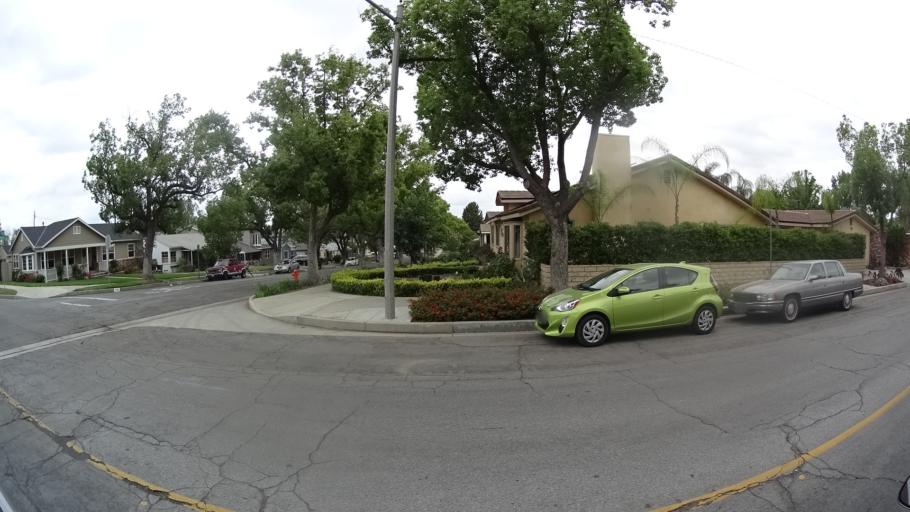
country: US
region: California
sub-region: Los Angeles County
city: Burbank
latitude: 34.2003
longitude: -118.3242
